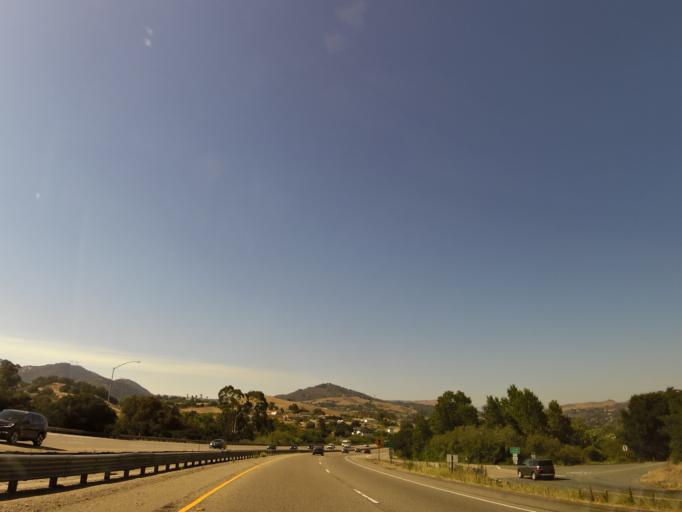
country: US
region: California
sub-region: San Luis Obispo County
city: Avila Beach
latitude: 35.1819
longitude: -120.7009
